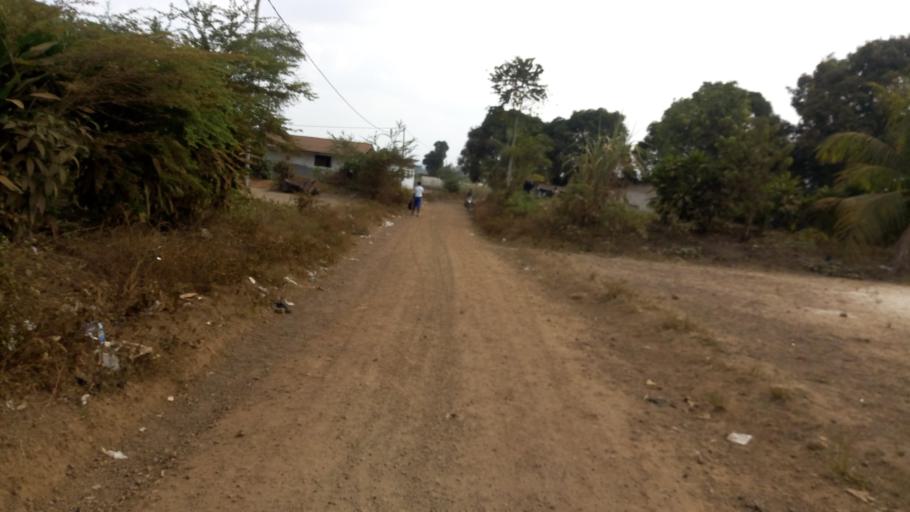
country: SL
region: Southern Province
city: Mogbwemo
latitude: 7.7795
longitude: -12.2988
